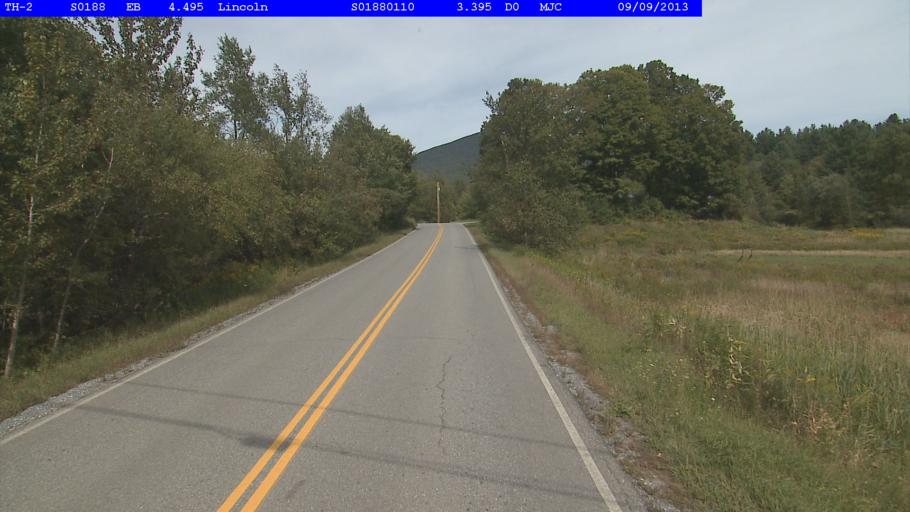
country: US
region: Vermont
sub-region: Addison County
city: Bristol
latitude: 44.0956
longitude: -72.9818
